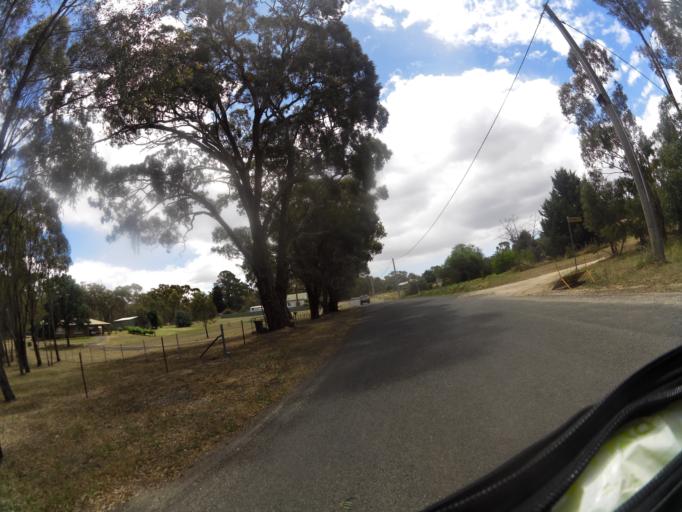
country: AU
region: Victoria
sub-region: Mount Alexander
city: Castlemaine
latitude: -37.0252
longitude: 144.2417
